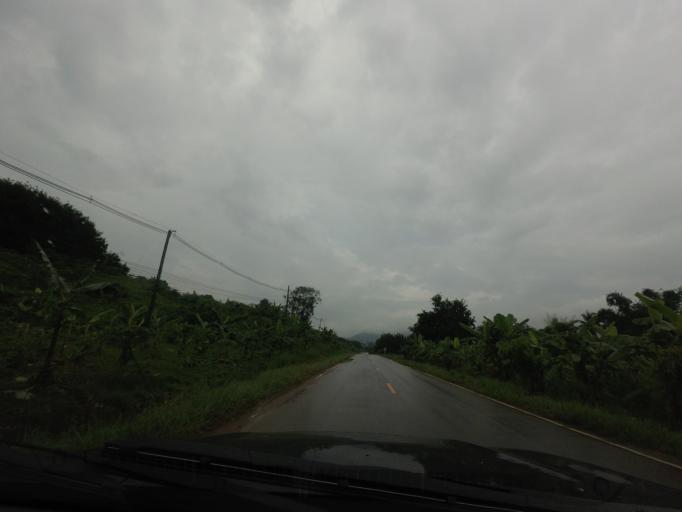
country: TH
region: Nong Khai
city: Sangkhom
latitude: 18.2118
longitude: 102.0887
